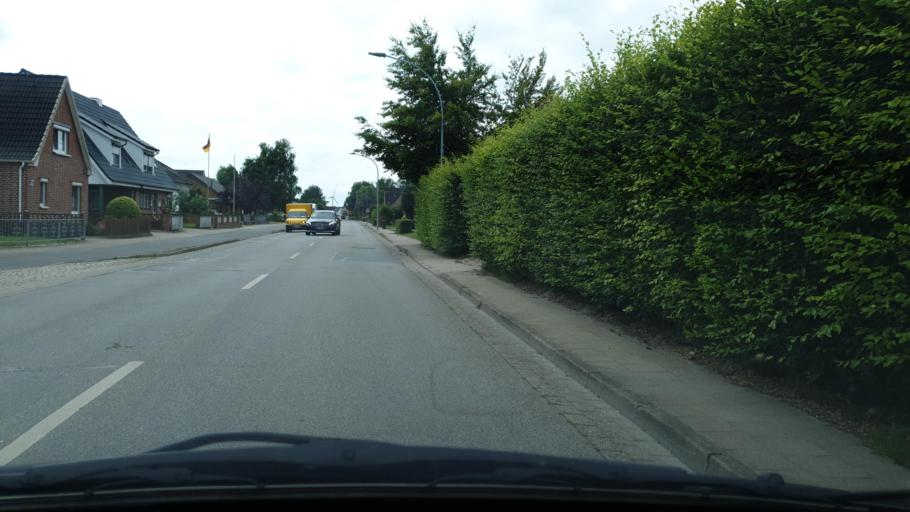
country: DE
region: Schleswig-Holstein
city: Marnerdeich
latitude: 53.9497
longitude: 9.0009
